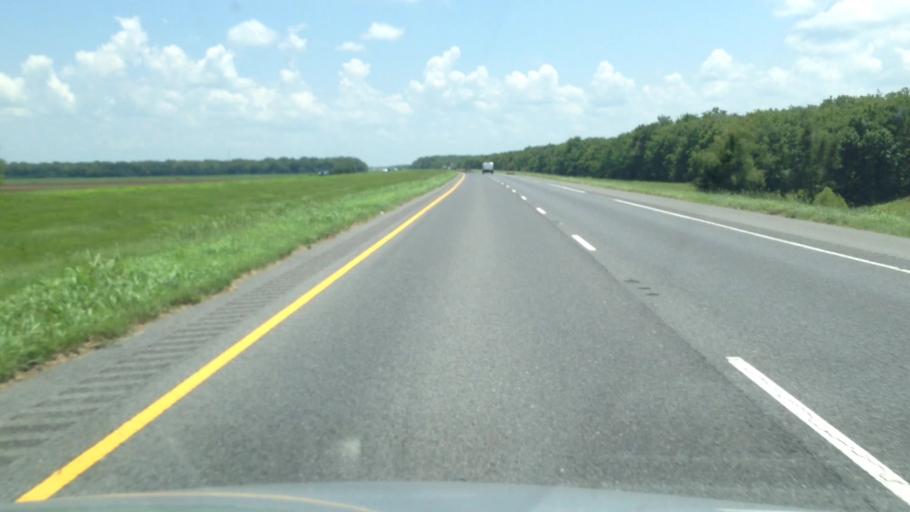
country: US
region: Louisiana
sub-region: Evangeline Parish
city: Ville Platte
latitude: 30.8060
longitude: -92.2143
